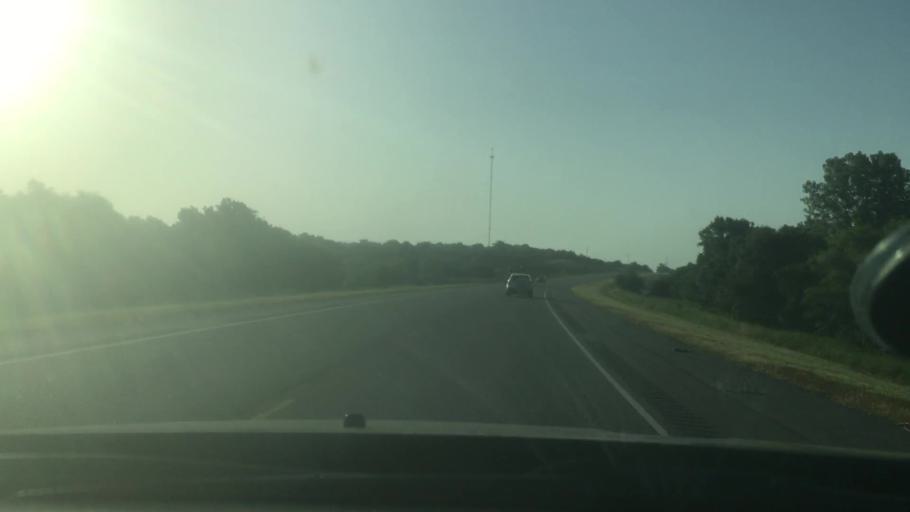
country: US
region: Oklahoma
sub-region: Pontotoc County
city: Ada
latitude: 34.6409
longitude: -96.4876
